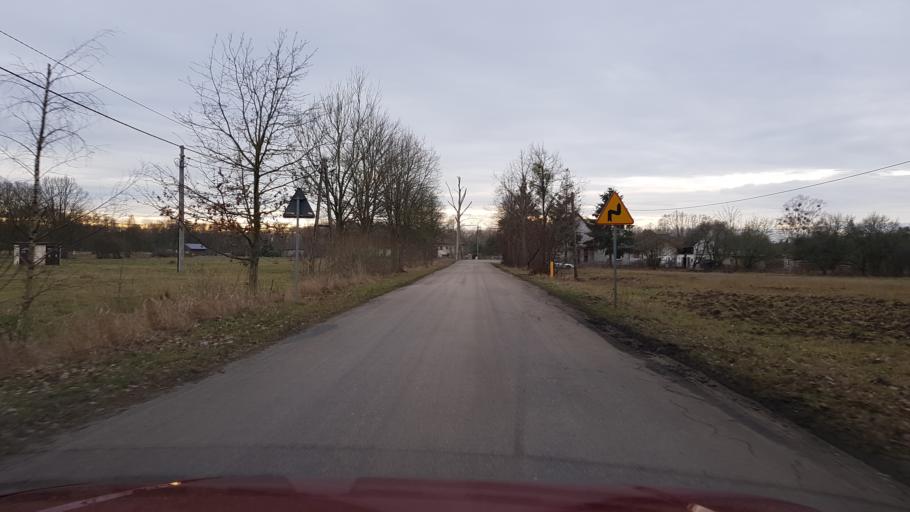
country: PL
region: West Pomeranian Voivodeship
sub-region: Powiat policki
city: Police
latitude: 53.5583
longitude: 14.4843
